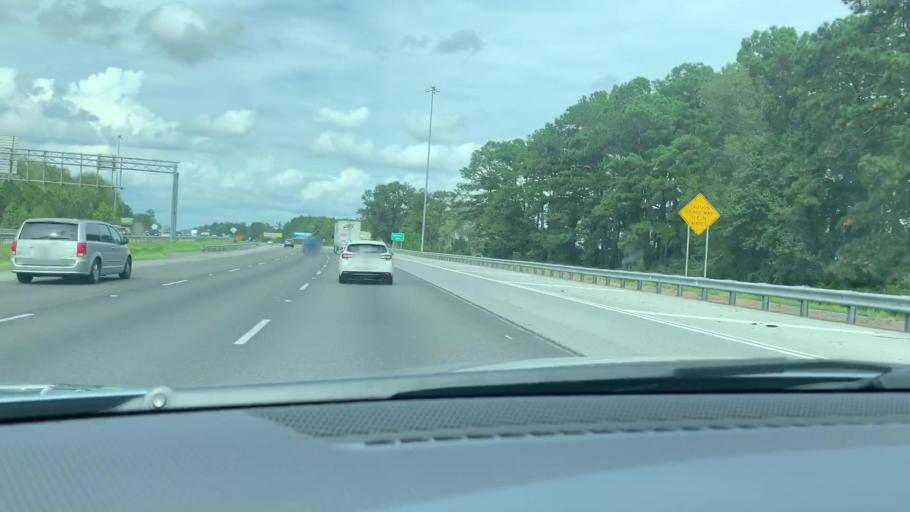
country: US
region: Georgia
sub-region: Liberty County
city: Midway
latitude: 31.6575
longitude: -81.3932
